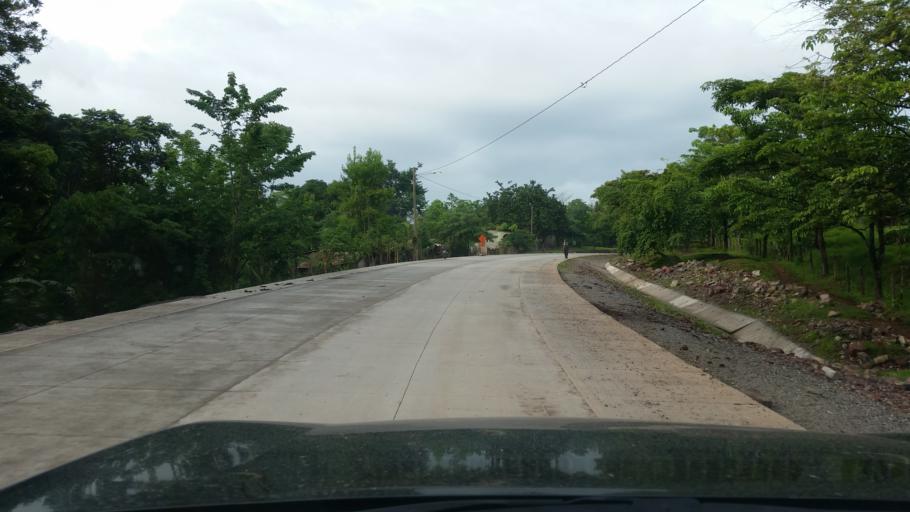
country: NI
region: Matagalpa
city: Rio Blanco
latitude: 13.1191
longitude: -85.0597
